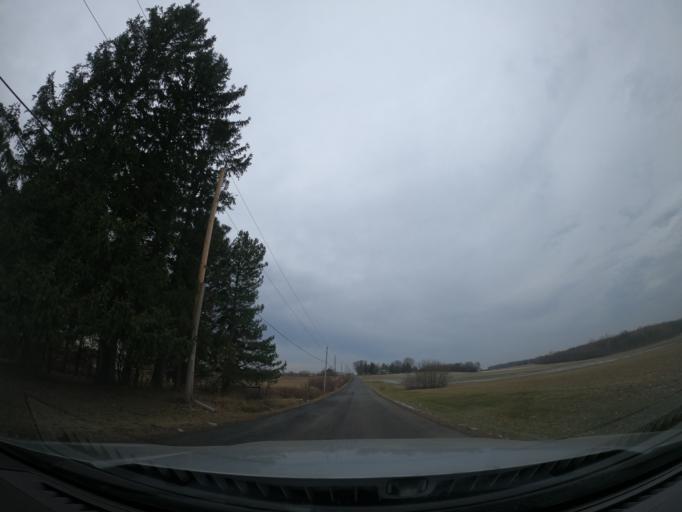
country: US
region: New York
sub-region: Cayuga County
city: Melrose Park
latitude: 42.8398
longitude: -76.5452
